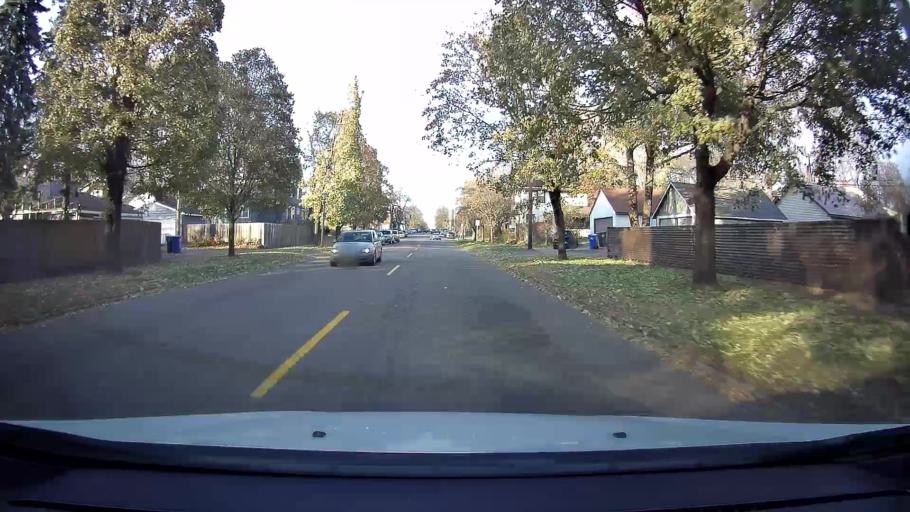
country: US
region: Minnesota
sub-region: Ramsey County
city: Falcon Heights
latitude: 44.9381
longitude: -93.1569
